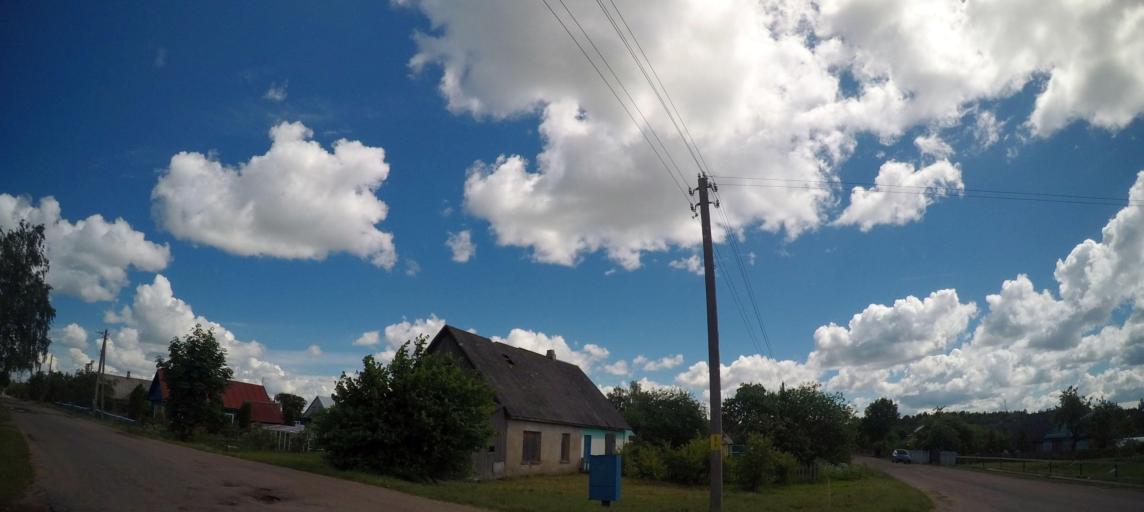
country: BY
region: Grodnenskaya
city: Hal'shany
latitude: 54.1634
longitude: 26.0893
